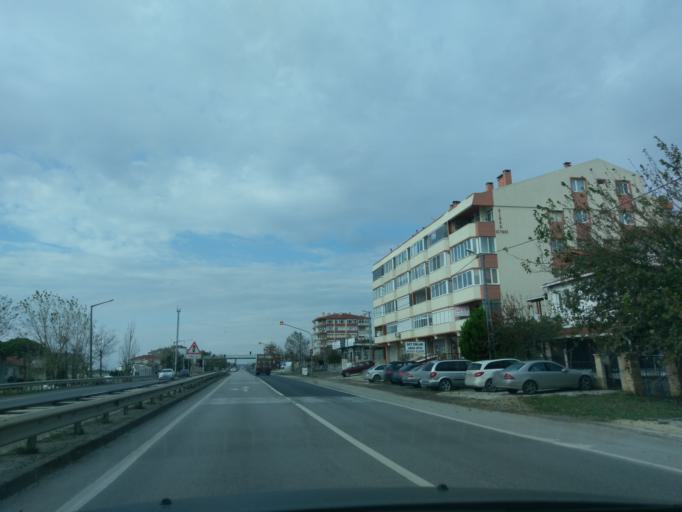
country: TR
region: Istanbul
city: Celaliye
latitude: 41.0434
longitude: 28.4161
